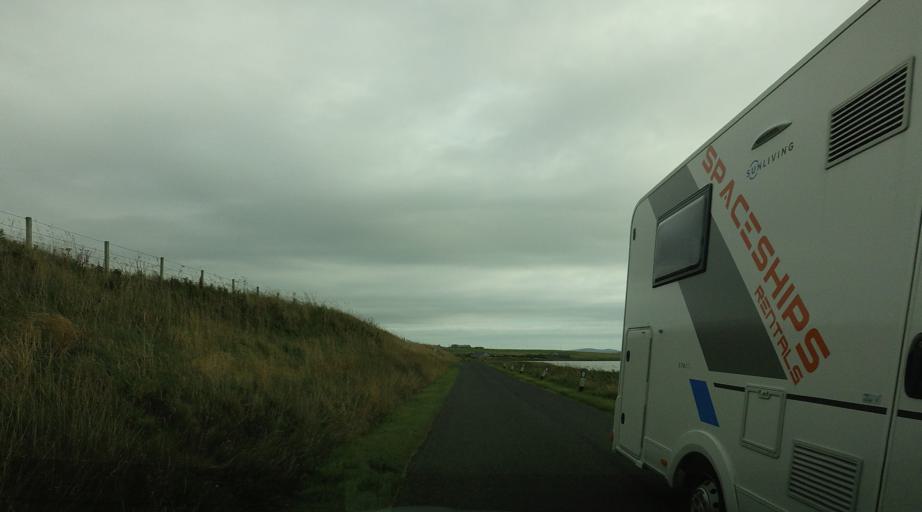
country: GB
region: Scotland
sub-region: Orkney Islands
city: Stromness
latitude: 59.0439
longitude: -3.3162
